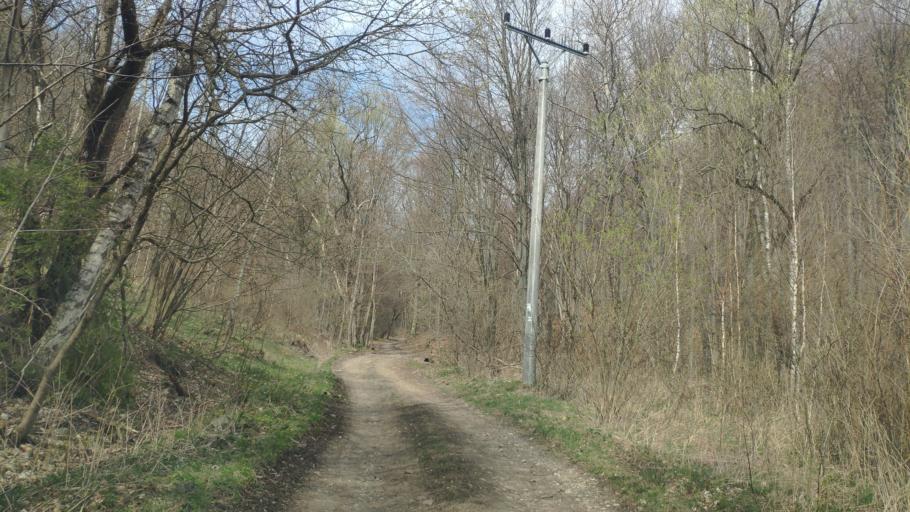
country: SK
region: Kosicky
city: Moldava nad Bodvou
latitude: 48.7497
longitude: 21.0276
